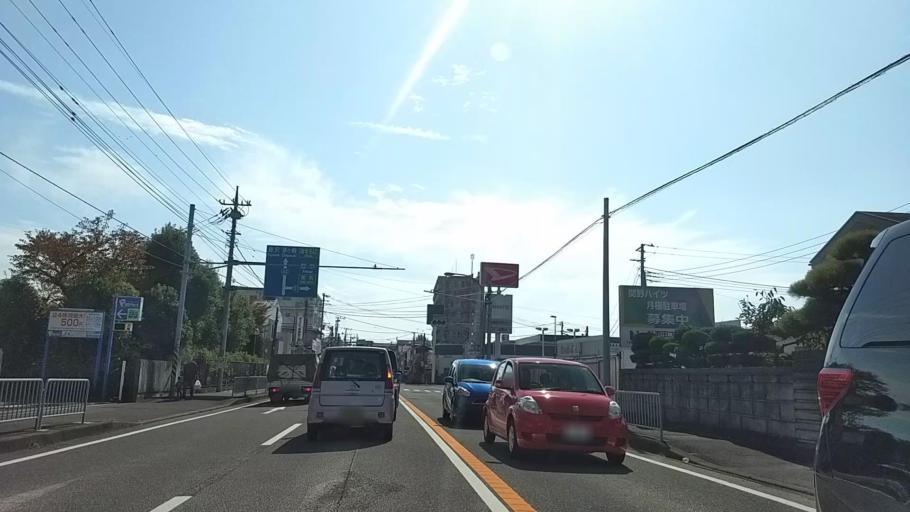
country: JP
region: Kanagawa
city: Atsugi
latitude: 35.4456
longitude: 139.3780
